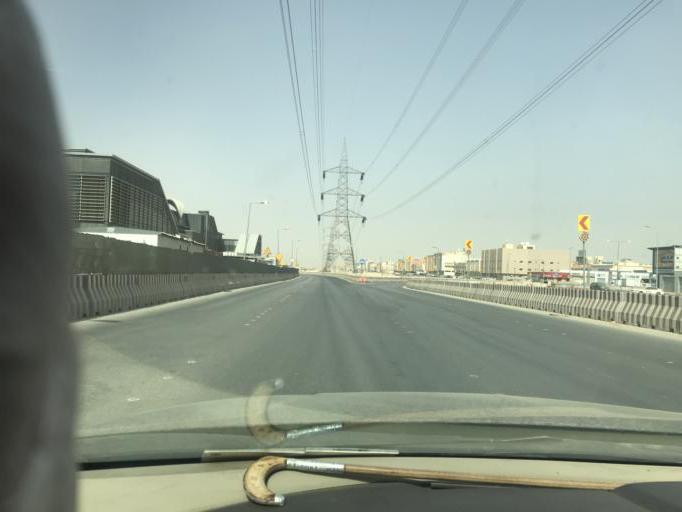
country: SA
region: Ar Riyad
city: Riyadh
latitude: 24.8004
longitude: 46.6948
